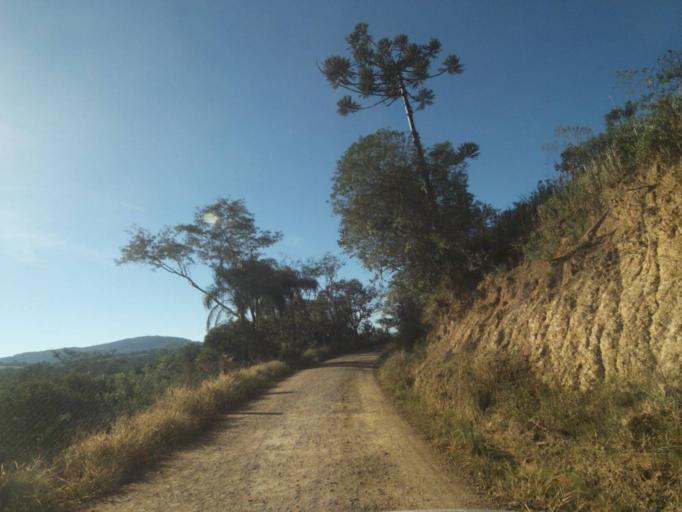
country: BR
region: Parana
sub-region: Tibagi
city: Tibagi
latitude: -24.5491
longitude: -50.5163
